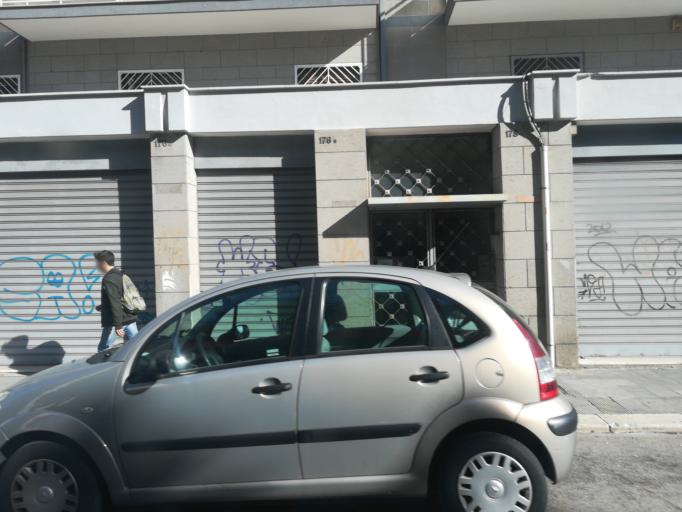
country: IT
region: Apulia
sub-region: Provincia di Bari
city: Bari
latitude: 41.1120
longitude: 16.8765
